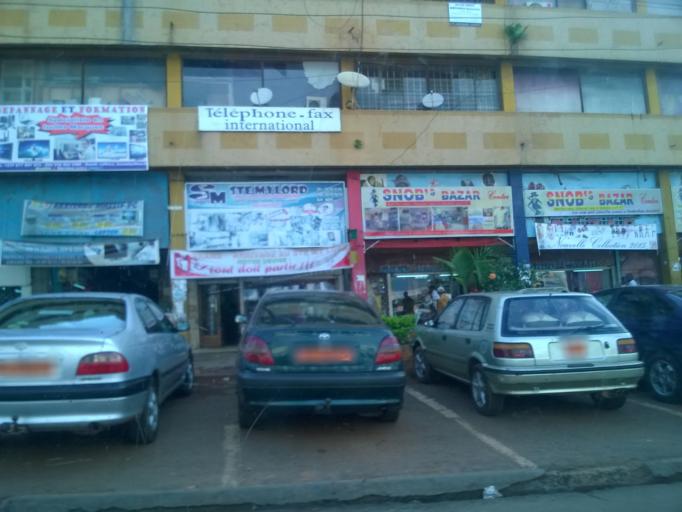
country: CM
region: Centre
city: Yaounde
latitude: 3.8665
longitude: 11.5171
